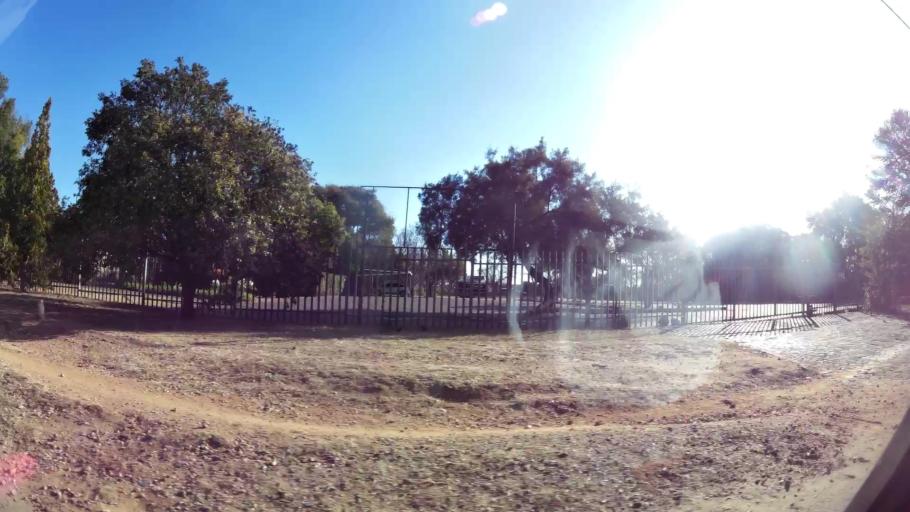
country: ZA
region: Gauteng
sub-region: City of Johannesburg Metropolitan Municipality
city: Roodepoort
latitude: -26.0836
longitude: 27.9635
